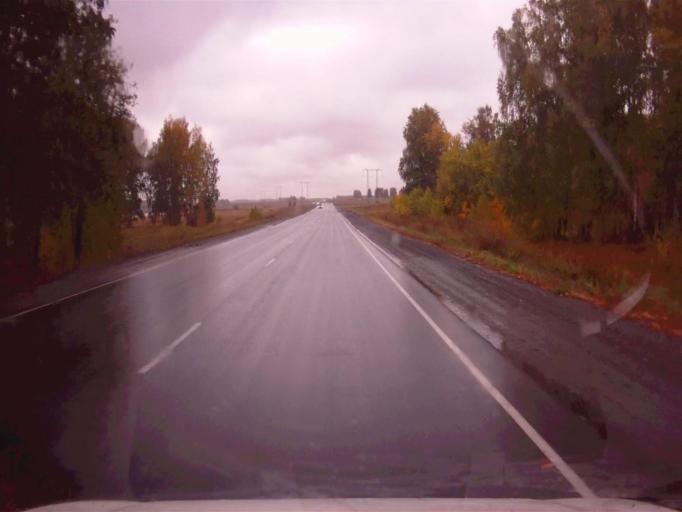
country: RU
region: Chelyabinsk
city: Roshchino
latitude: 55.3879
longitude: 61.1281
